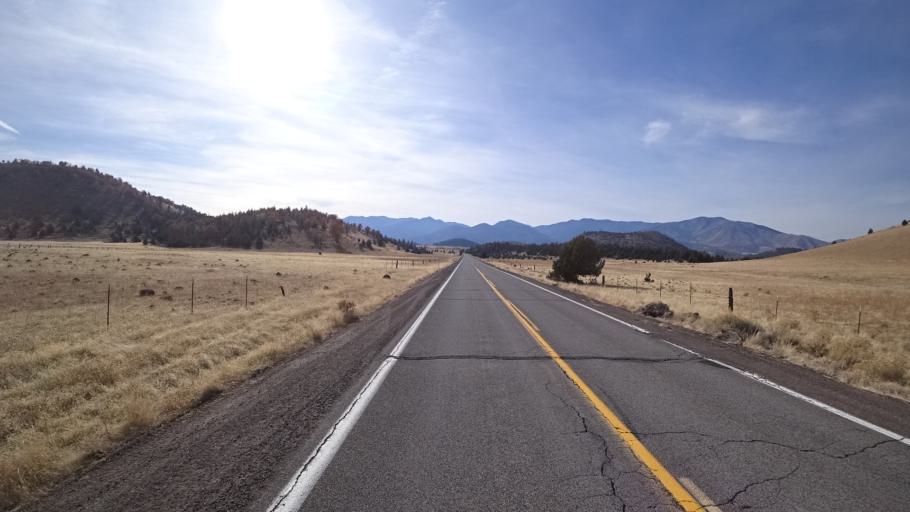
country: US
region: California
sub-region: Siskiyou County
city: Weed
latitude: 41.4920
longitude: -122.4040
